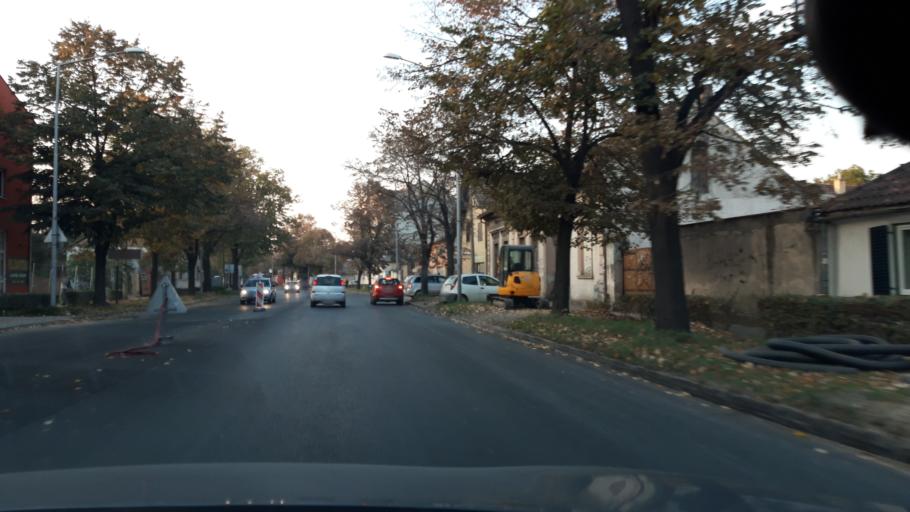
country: RS
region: Autonomna Pokrajina Vojvodina
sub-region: Juznobacki Okrug
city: Petrovaradin
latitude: 45.2458
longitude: 19.8801
